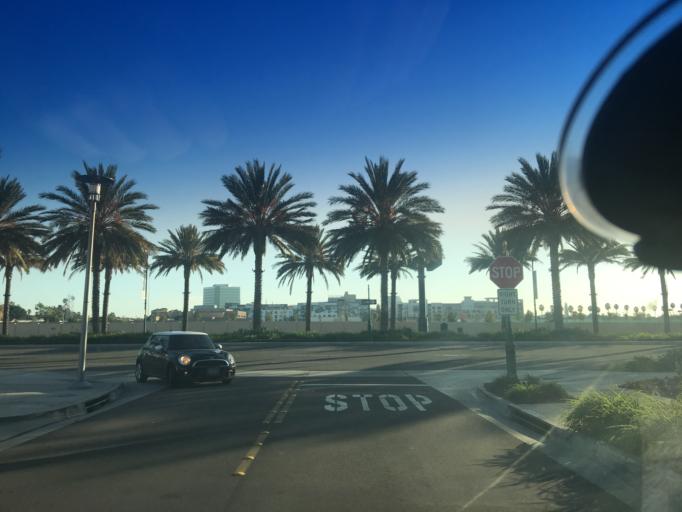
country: US
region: California
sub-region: Orange County
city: Anaheim
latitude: 33.8041
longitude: -117.8915
